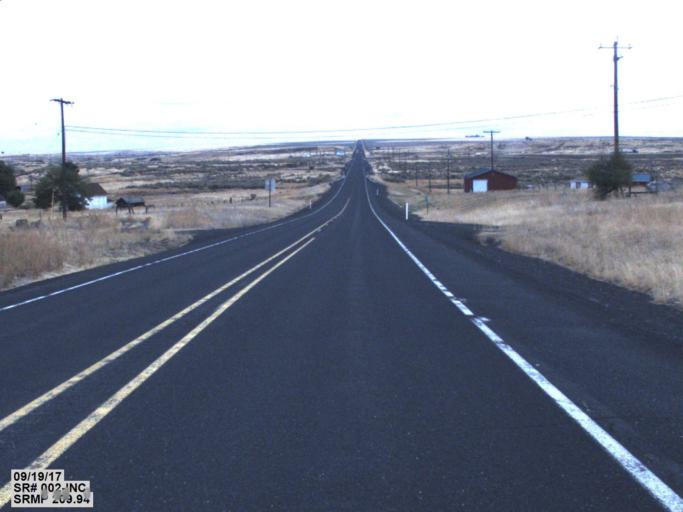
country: US
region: Washington
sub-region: Okanogan County
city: Coulee Dam
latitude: 47.7063
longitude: -118.9378
